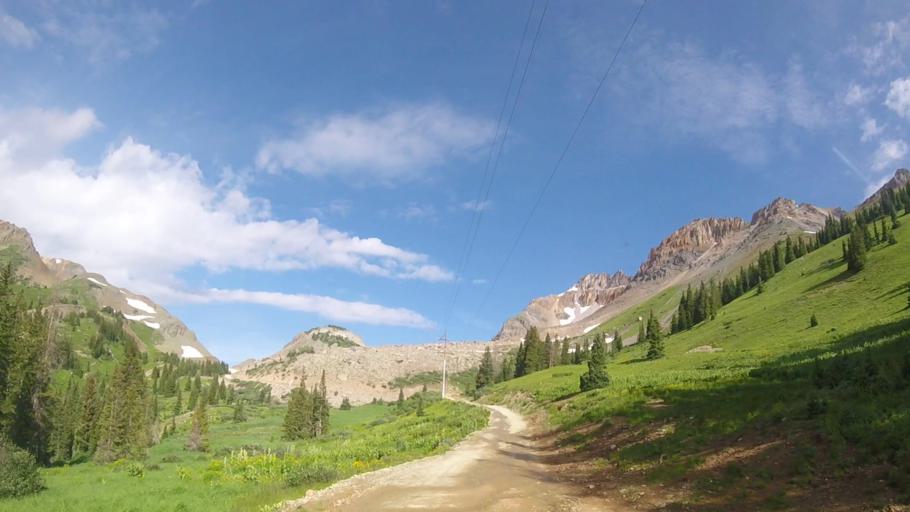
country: US
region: Colorado
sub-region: San Miguel County
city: Telluride
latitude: 37.8502
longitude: -107.7702
